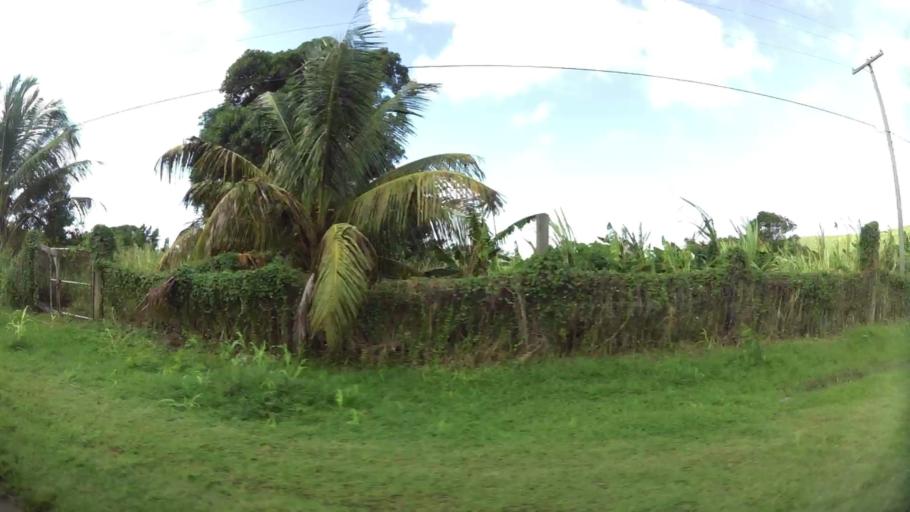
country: AG
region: Saint Mary
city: Bolands
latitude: 17.0721
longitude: -61.8677
